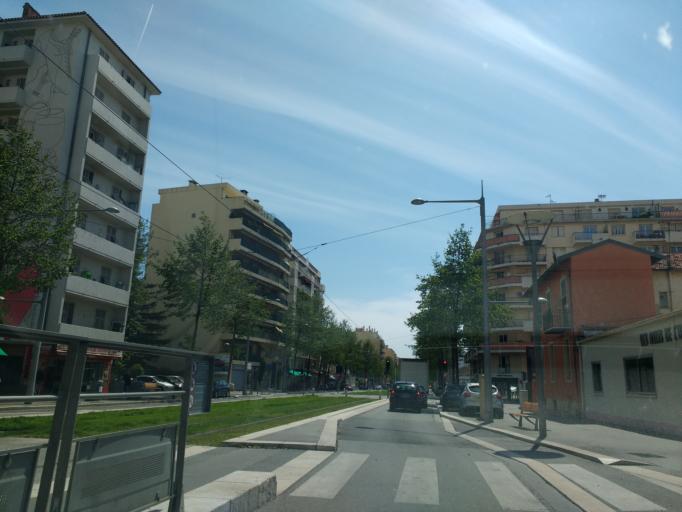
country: FR
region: Provence-Alpes-Cote d'Azur
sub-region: Departement des Alpes-Maritimes
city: Villefranche-sur-Mer
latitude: 43.7146
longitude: 7.2928
